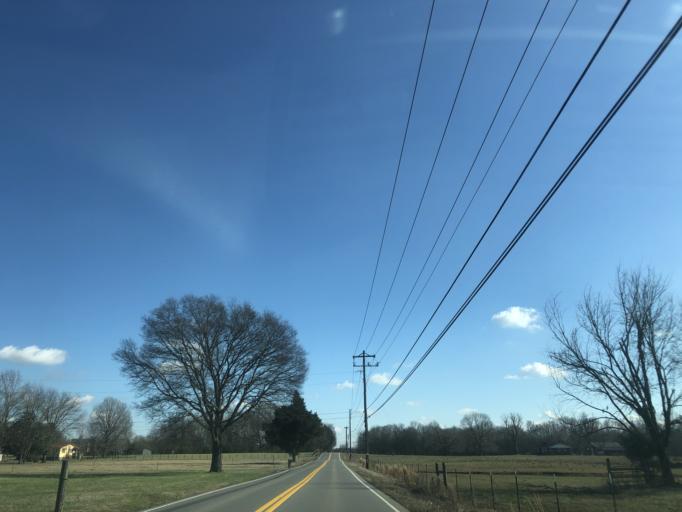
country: US
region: Tennessee
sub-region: Rutherford County
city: Smyrna
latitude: 35.9832
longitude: -86.4143
